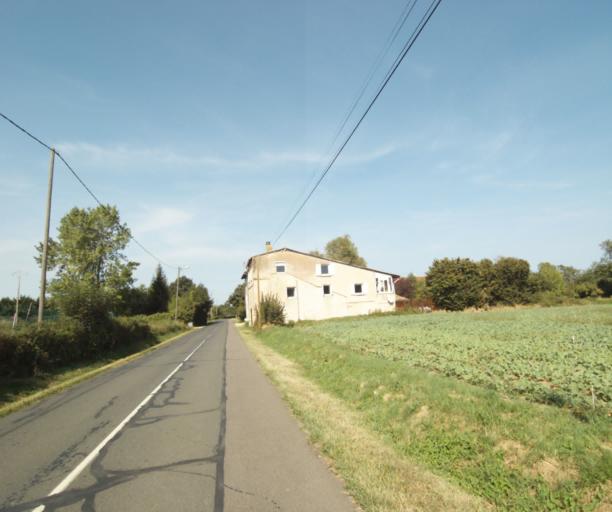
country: FR
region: Bourgogne
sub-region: Departement de Saone-et-Loire
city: Tournus
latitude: 46.5439
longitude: 4.8931
